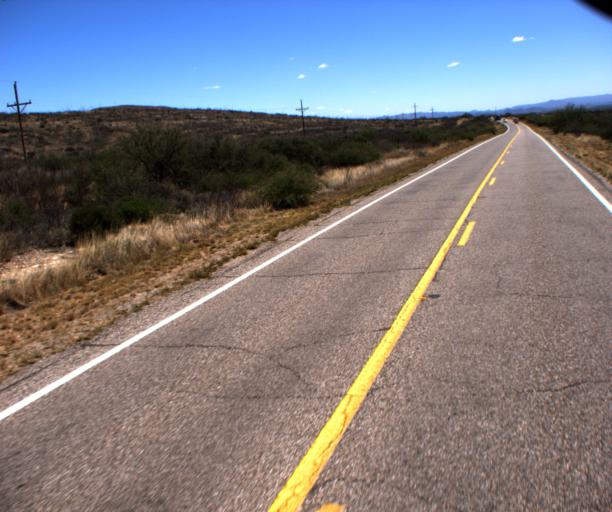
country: US
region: Arizona
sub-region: Cochise County
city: Huachuca City
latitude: 31.6926
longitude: -110.4059
